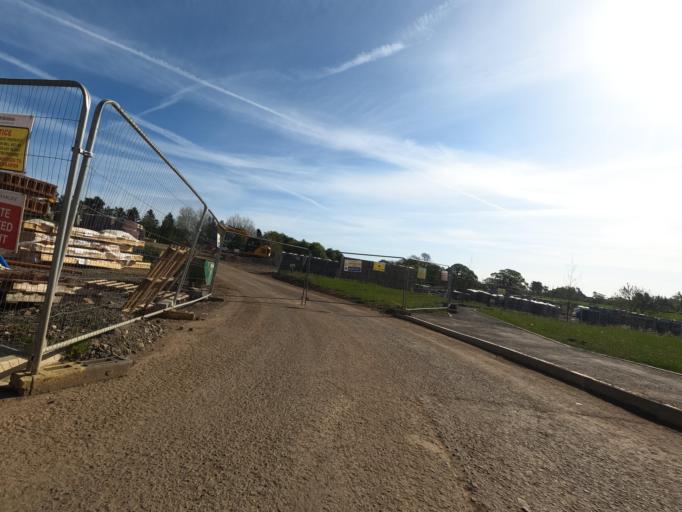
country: GB
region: England
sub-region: Northumberland
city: Morpeth
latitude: 55.1812
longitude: -1.7097
